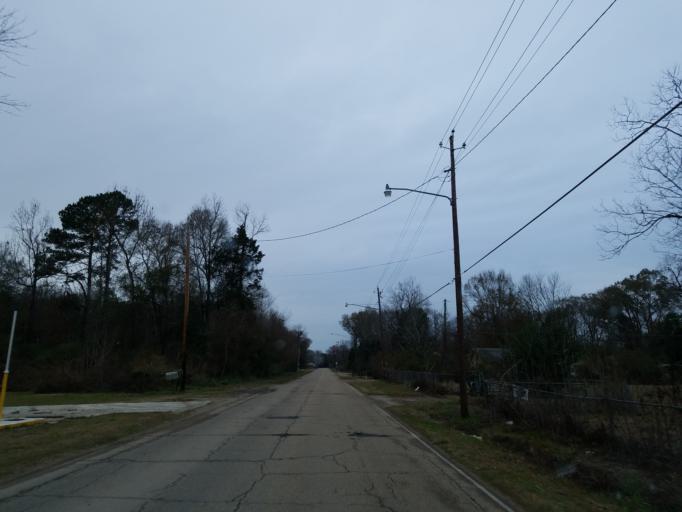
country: US
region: Mississippi
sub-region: Forrest County
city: Hattiesburg
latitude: 31.2954
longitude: -89.2709
